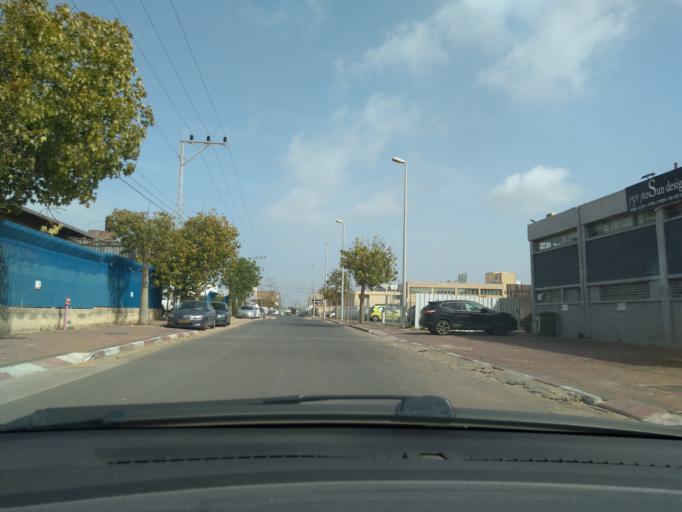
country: IL
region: Central District
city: Even Yehuda
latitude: 32.2799
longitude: 34.8591
